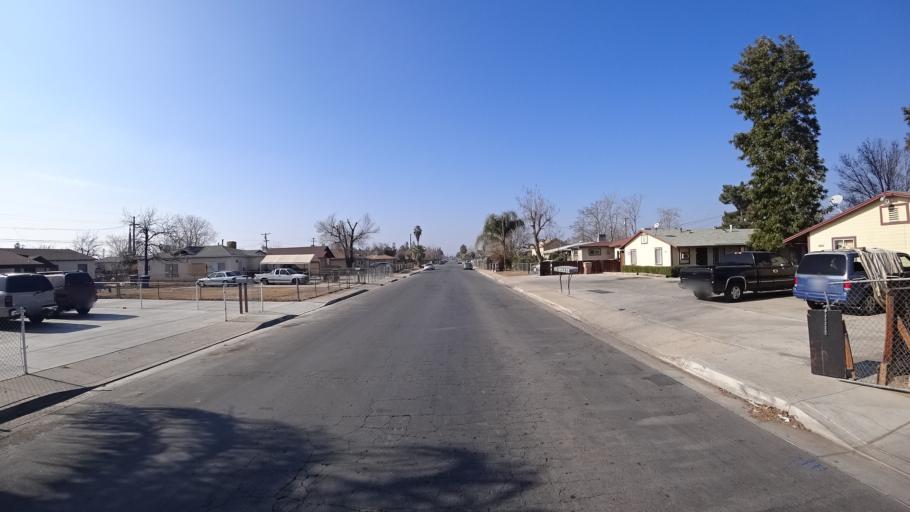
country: US
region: California
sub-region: Kern County
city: Bakersfield
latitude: 35.3648
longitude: -118.9871
